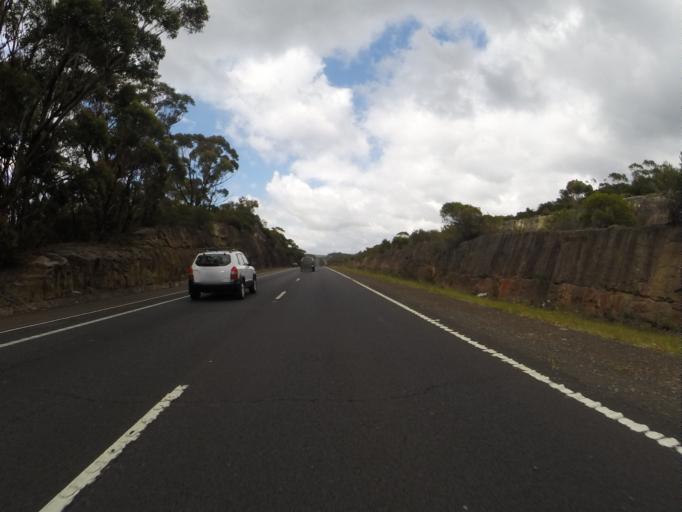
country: AU
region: New South Wales
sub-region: Wollongong
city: Helensburgh
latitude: -34.2095
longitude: 150.9618
